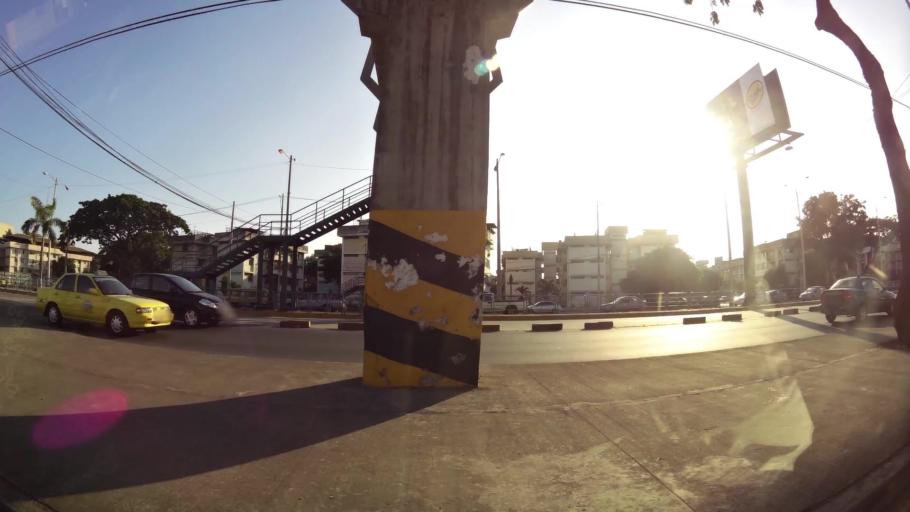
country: EC
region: Guayas
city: Guayaquil
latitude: -2.2262
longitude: -79.8980
